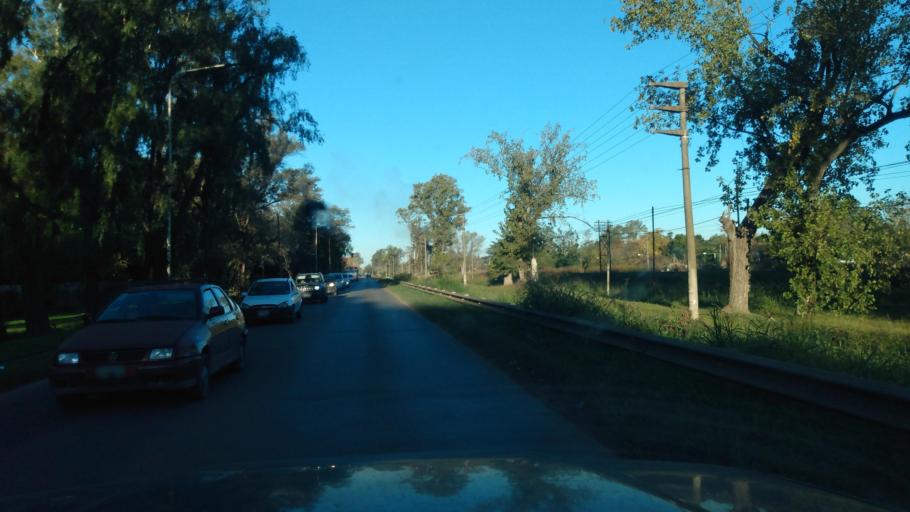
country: AR
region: Buenos Aires
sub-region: Partido de General Rodriguez
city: General Rodriguez
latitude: -34.6343
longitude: -58.8465
